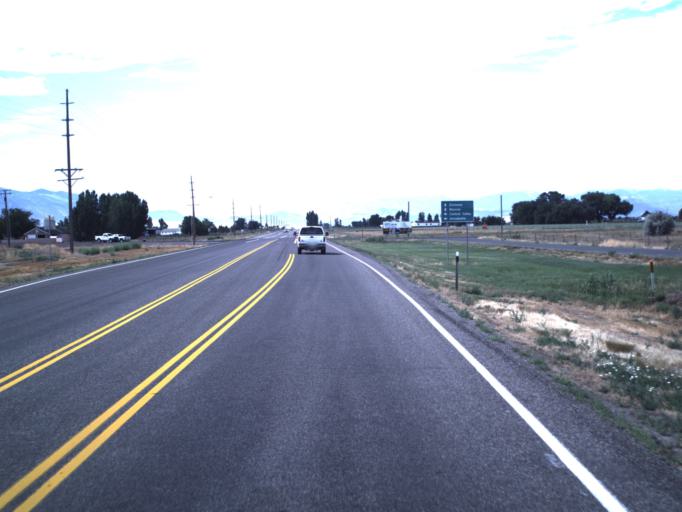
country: US
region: Utah
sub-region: Sevier County
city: Richfield
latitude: 38.7257
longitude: -112.0995
